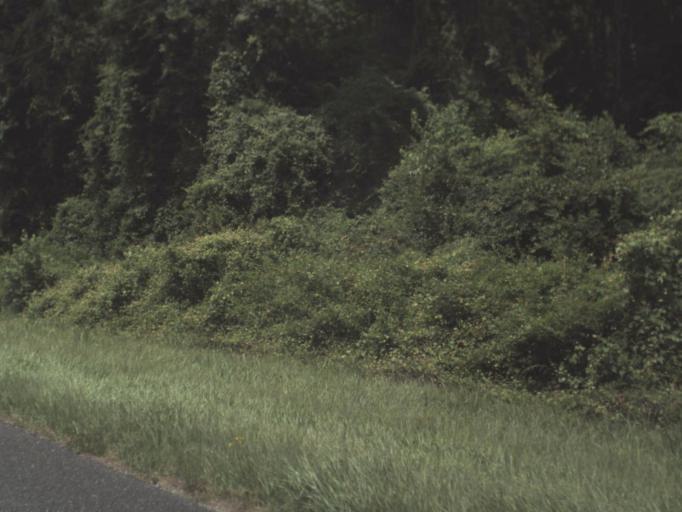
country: US
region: Florida
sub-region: Taylor County
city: Perry
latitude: 30.2833
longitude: -83.7299
